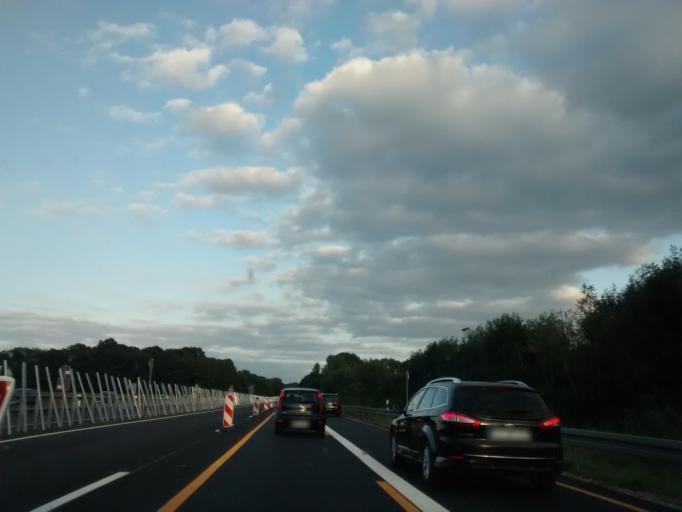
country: DE
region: Lower Saxony
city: Hasbergen
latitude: 52.2683
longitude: 7.9684
